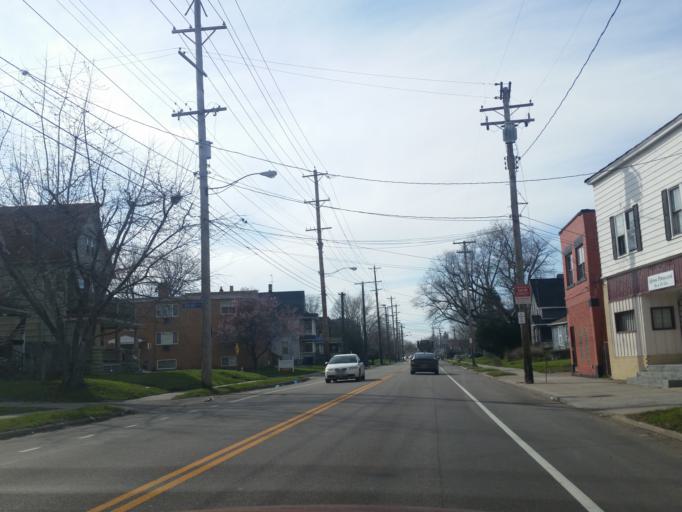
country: US
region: Ohio
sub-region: Cuyahoga County
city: Brooklyn
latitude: 41.4517
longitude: -81.7127
